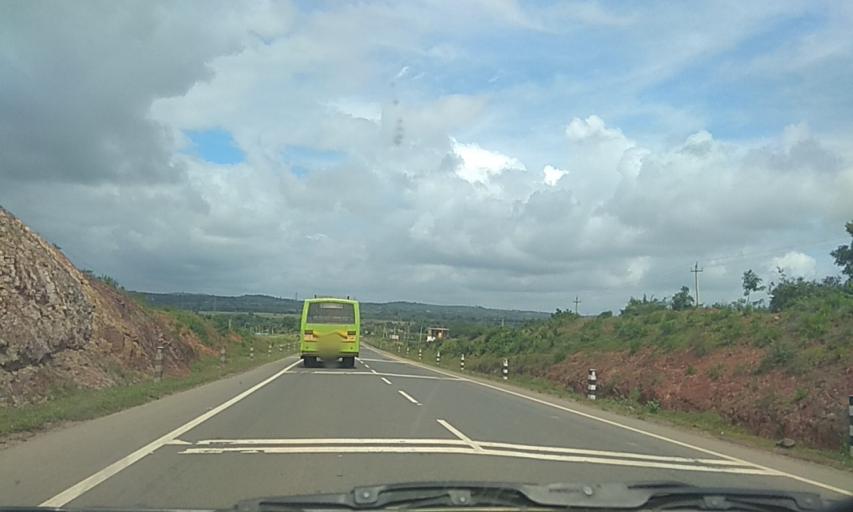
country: IN
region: Karnataka
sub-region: Dharwad
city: Hubli
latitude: 15.4032
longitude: 74.9940
